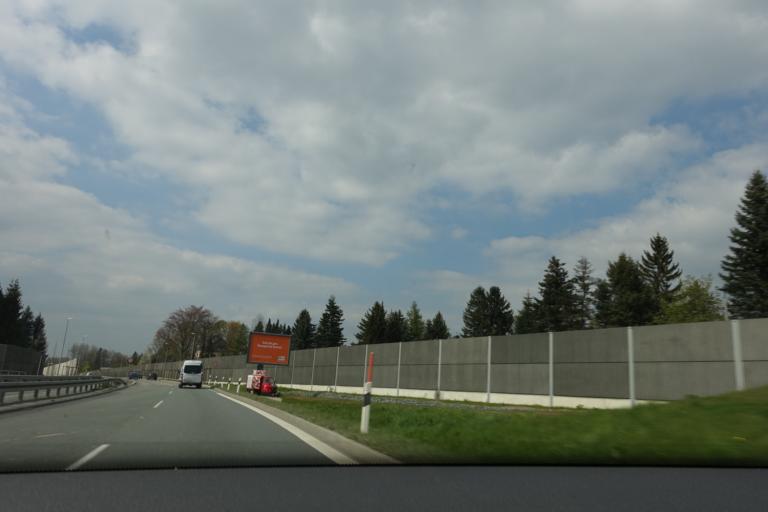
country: DE
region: Saxony
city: Hilbersdorf
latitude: 50.8052
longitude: 12.9716
